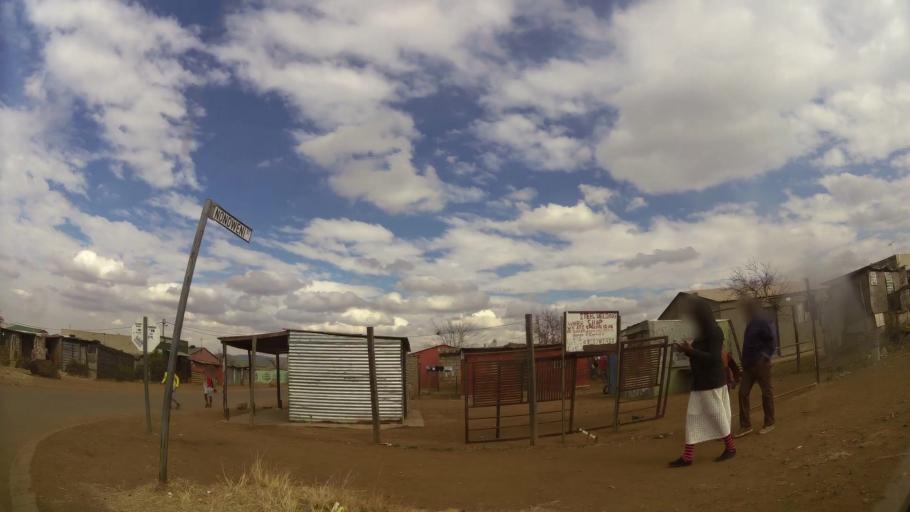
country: ZA
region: Gauteng
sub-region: Ekurhuleni Metropolitan Municipality
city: Germiston
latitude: -26.4018
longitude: 28.1652
